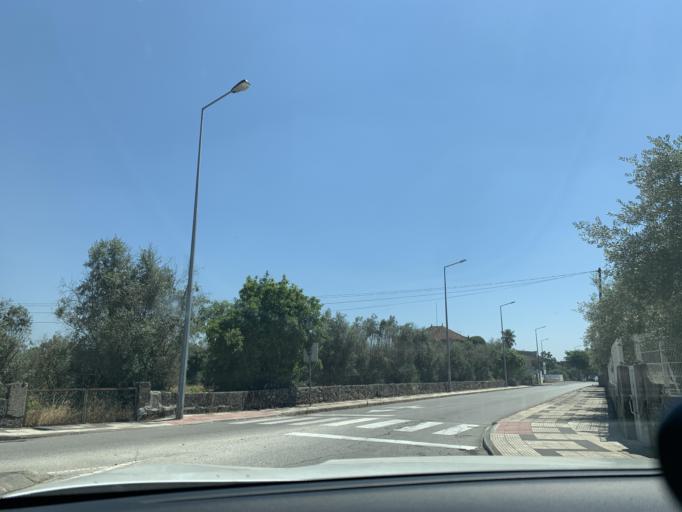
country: PT
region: Viseu
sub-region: Nelas
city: Nelas
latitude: 40.5395
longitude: -7.8458
